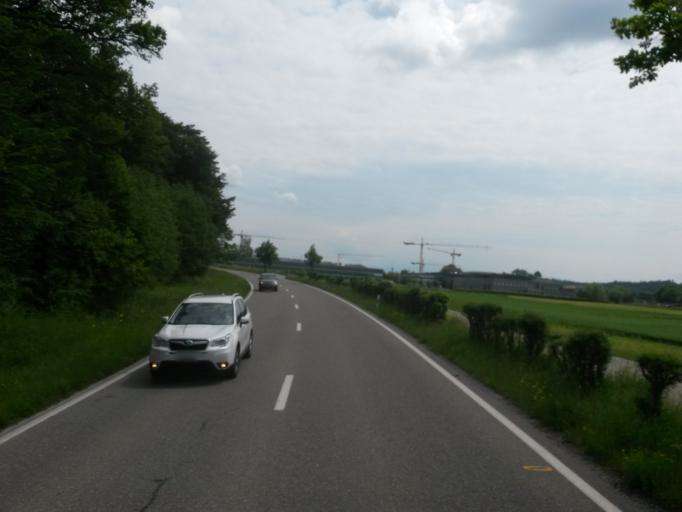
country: CH
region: Zurich
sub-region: Bezirk Pfaeffikon
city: Illnau / Unter-Illnau
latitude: 47.3988
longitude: 8.7336
